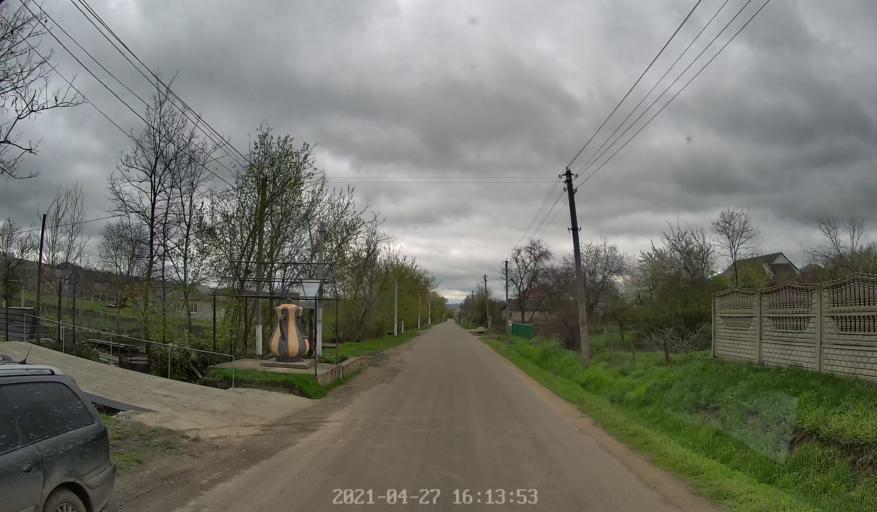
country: MD
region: Chisinau
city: Singera
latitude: 47.0062
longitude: 29.0139
